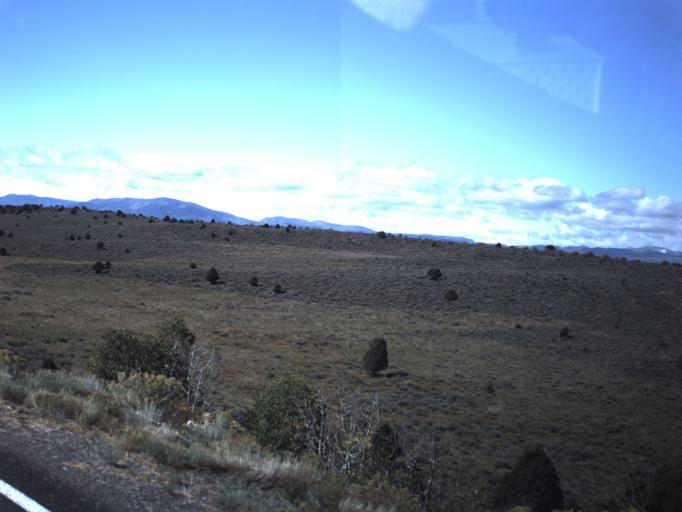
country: US
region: Utah
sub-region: Wayne County
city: Loa
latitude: 38.4918
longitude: -111.8153
